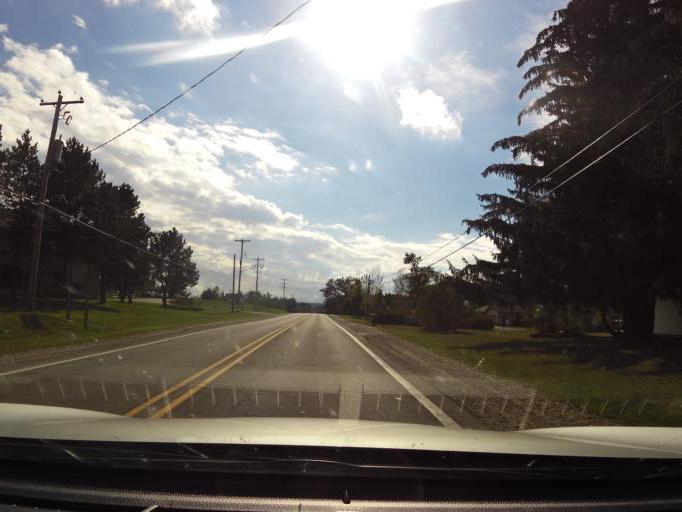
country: US
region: Michigan
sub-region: Roscommon County
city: Roscommon
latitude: 44.5053
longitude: -84.5847
